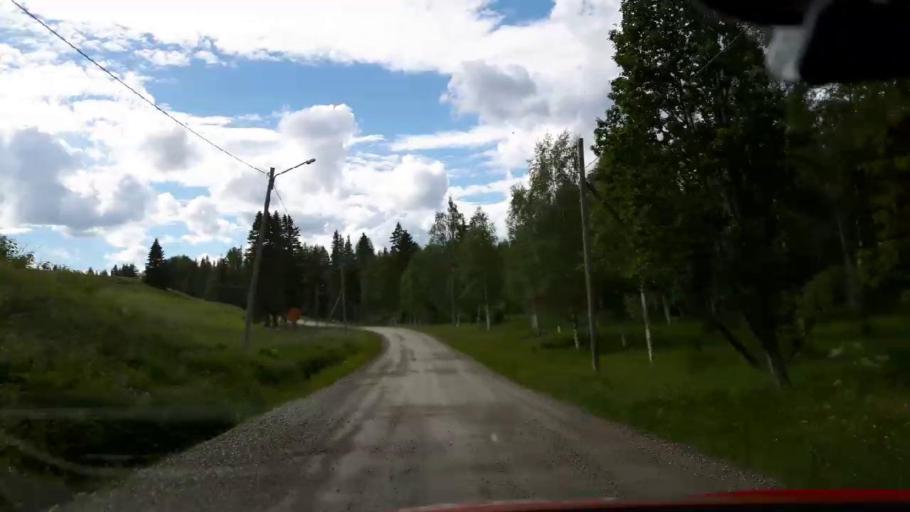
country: SE
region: Jaemtland
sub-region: Krokoms Kommun
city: Valla
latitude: 63.9045
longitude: 14.2099
